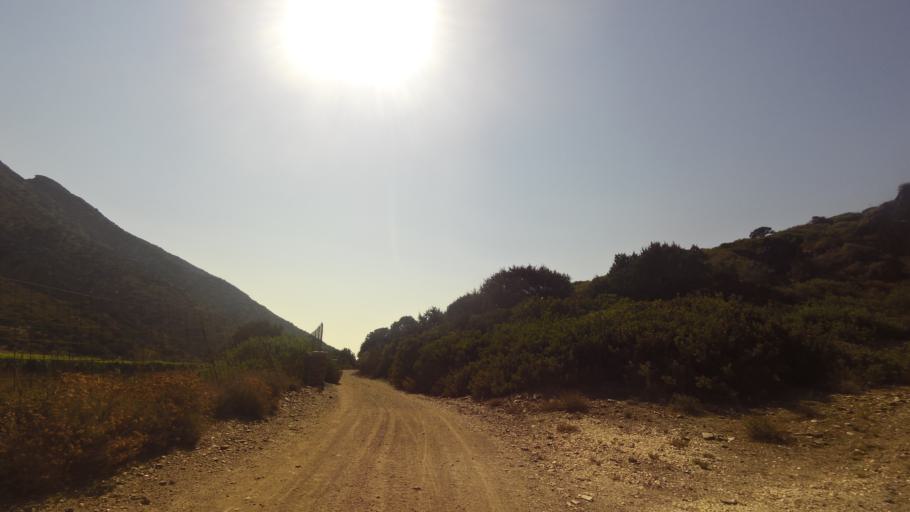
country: GR
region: South Aegean
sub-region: Nomos Kykladon
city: Antiparos
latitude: 37.0042
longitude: 25.0308
